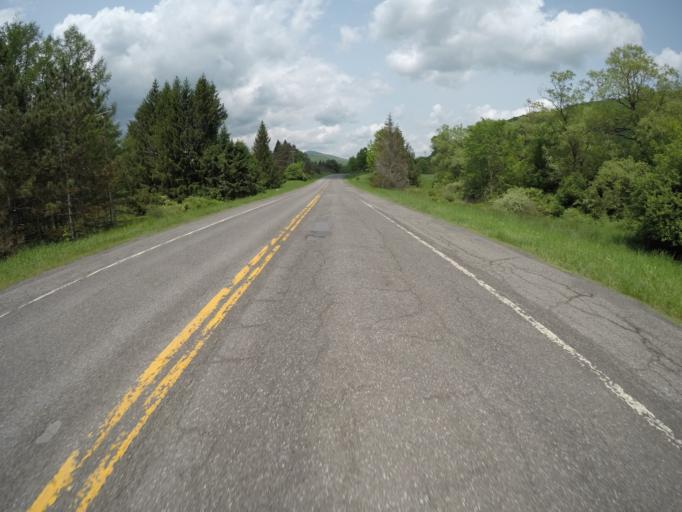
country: US
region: New York
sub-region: Delaware County
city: Stamford
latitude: 42.2512
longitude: -74.5953
